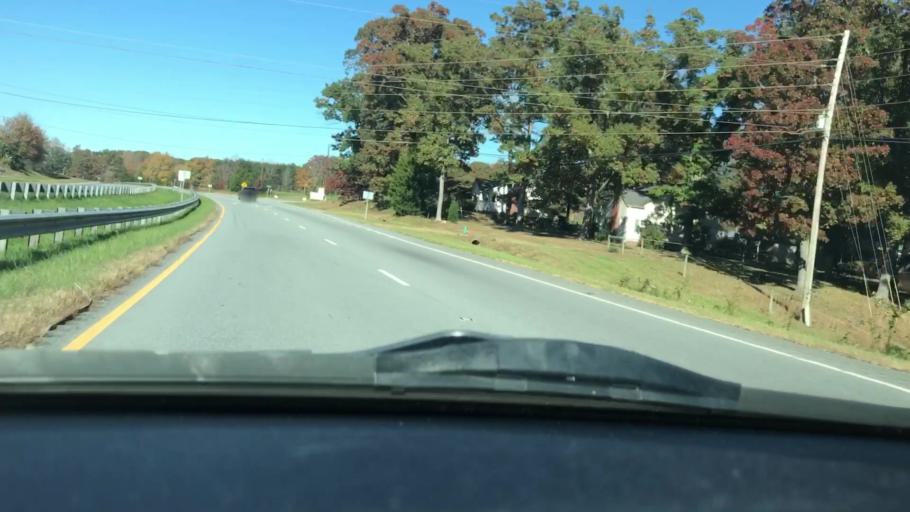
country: US
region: North Carolina
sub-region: Rockingham County
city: Madison
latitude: 36.3374
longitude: -79.9440
